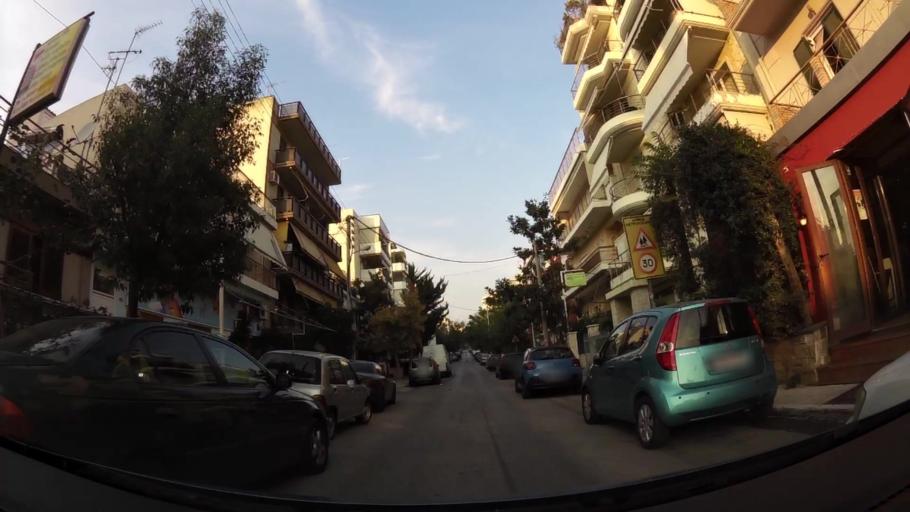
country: GR
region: Attica
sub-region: Nomarchia Athinas
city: Petroupolis
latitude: 38.0413
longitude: 23.6868
